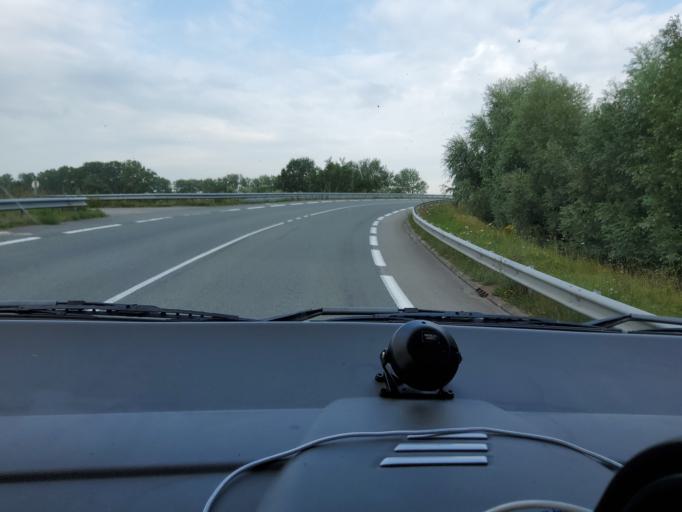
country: FR
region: Nord-Pas-de-Calais
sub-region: Departement du Nord
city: Brouckerque
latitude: 50.9552
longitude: 2.2719
